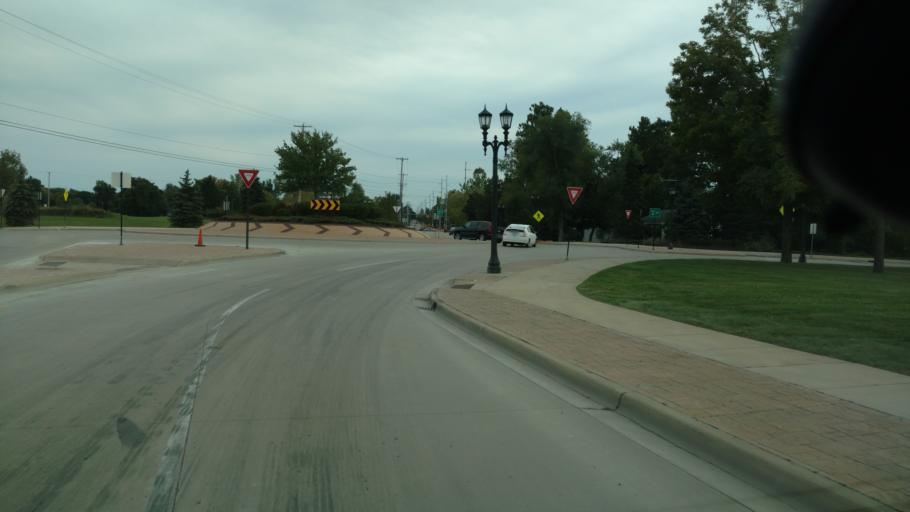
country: US
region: Michigan
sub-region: Ingham County
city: Lansing
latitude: 42.7632
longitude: -84.5230
